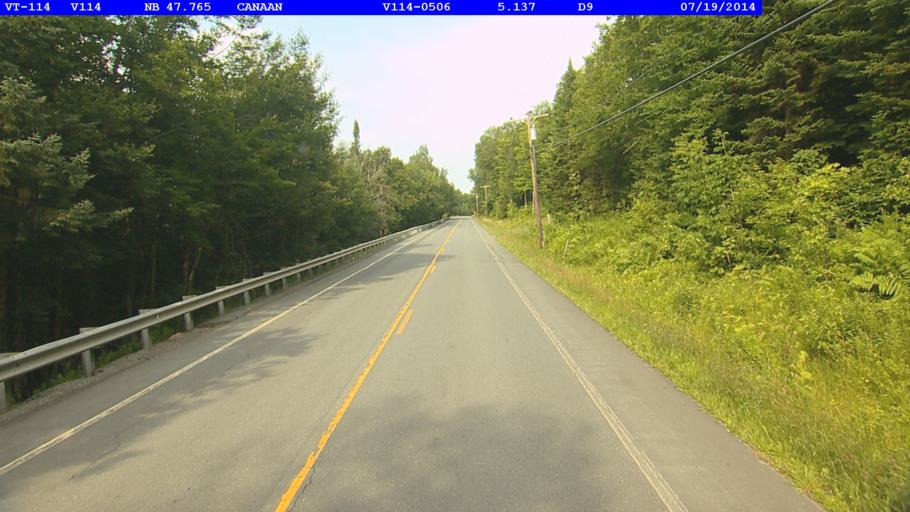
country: US
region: New Hampshire
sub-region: Coos County
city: Colebrook
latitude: 45.0072
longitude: -71.5922
